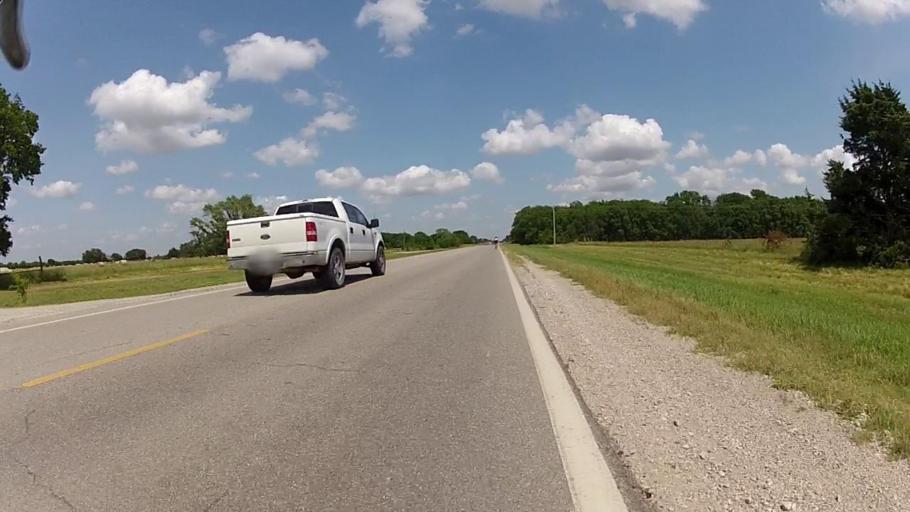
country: US
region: Kansas
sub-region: Labette County
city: Altamont
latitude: 37.1929
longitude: -95.2771
